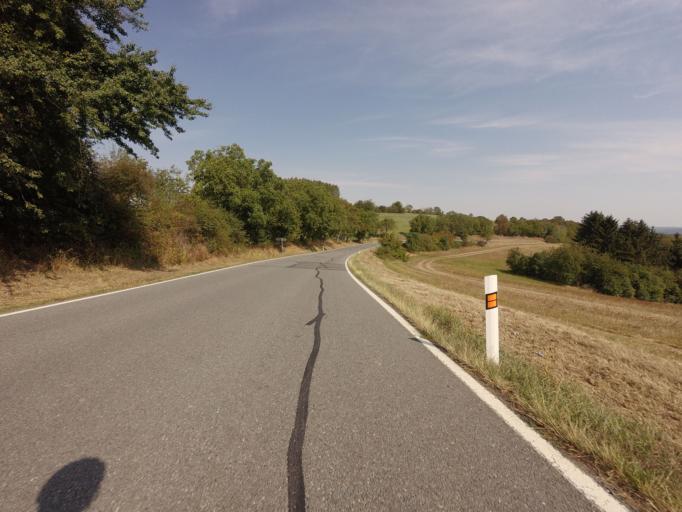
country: CZ
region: Central Bohemia
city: Petrovice
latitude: 49.5848
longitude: 14.3791
